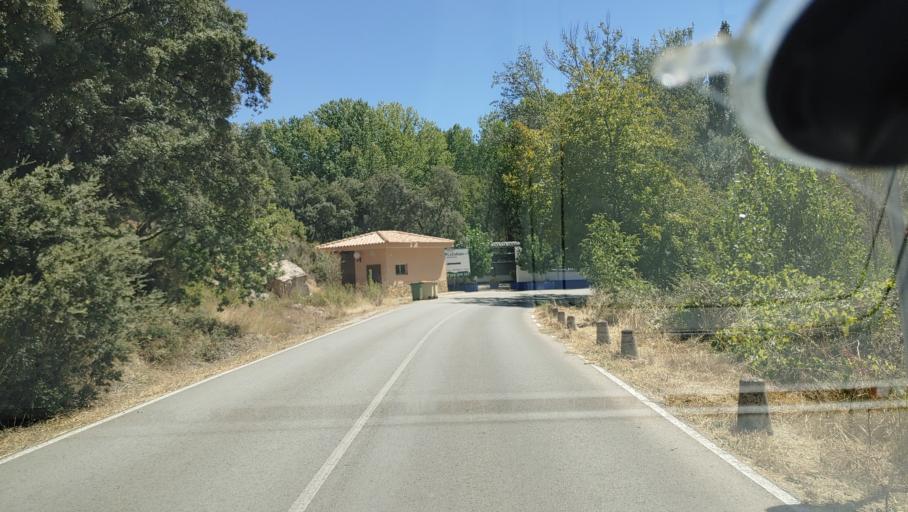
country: ES
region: Castille-La Mancha
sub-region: Provincia de Ciudad Real
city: Ruidera
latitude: 38.9612
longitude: -2.8582
